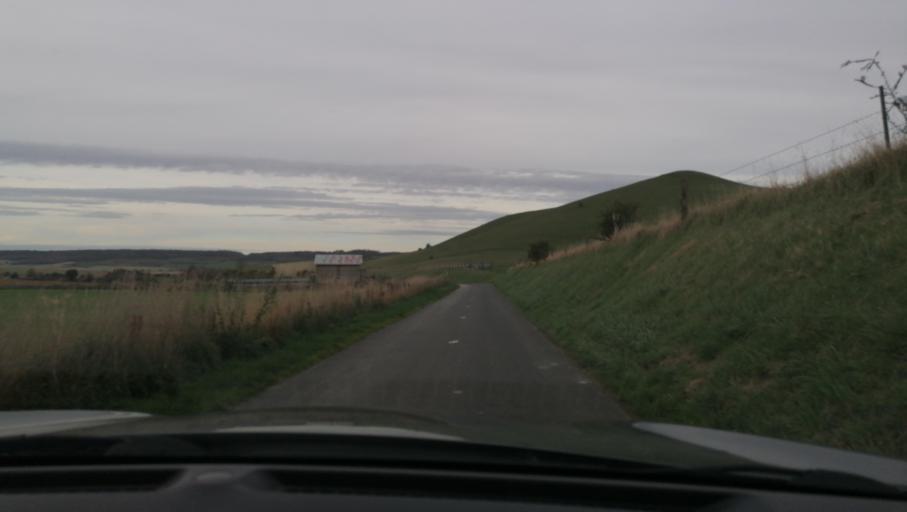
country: FR
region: Picardie
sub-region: Departement de la Somme
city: Bouttencourt
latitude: 49.8946
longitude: 1.6740
